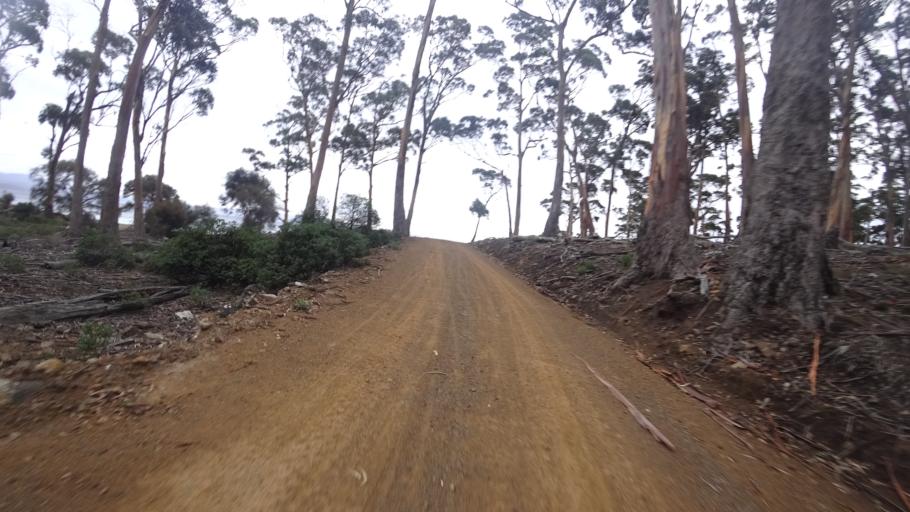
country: AU
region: Tasmania
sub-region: Sorell
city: Sorell
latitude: -42.6103
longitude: 148.0469
